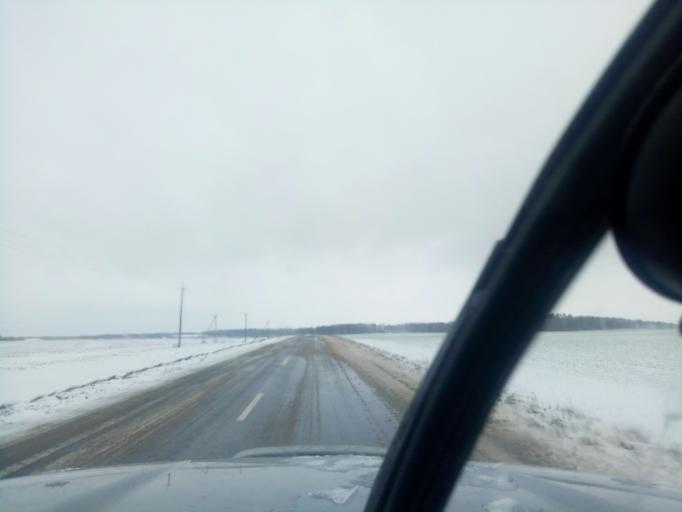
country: BY
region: Minsk
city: Tsimkavichy
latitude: 53.0447
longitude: 26.8531
